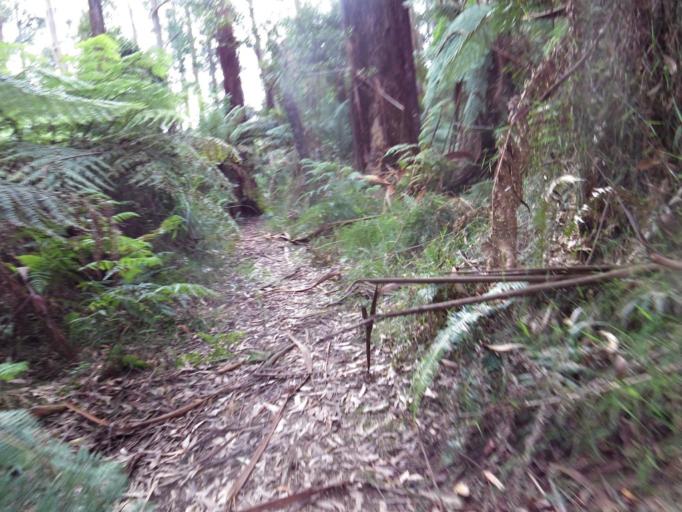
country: AU
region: Victoria
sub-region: Yarra Ranges
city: Healesville
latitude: -37.5396
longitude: 145.4805
